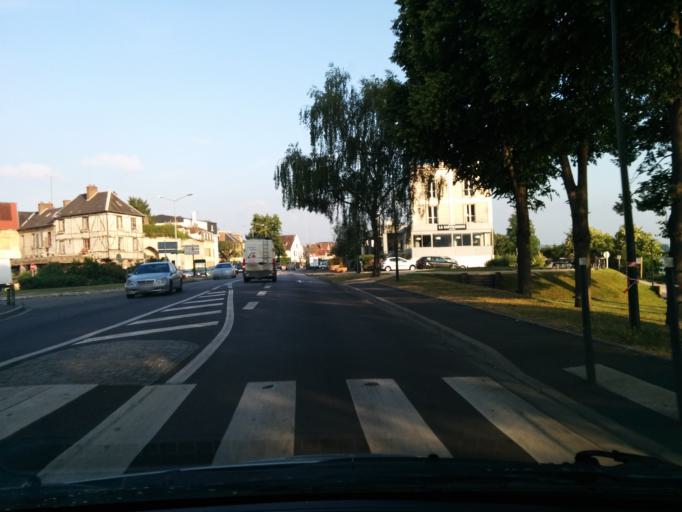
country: FR
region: Haute-Normandie
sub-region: Departement de l'Eure
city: Vernon
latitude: 49.0959
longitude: 1.4845
